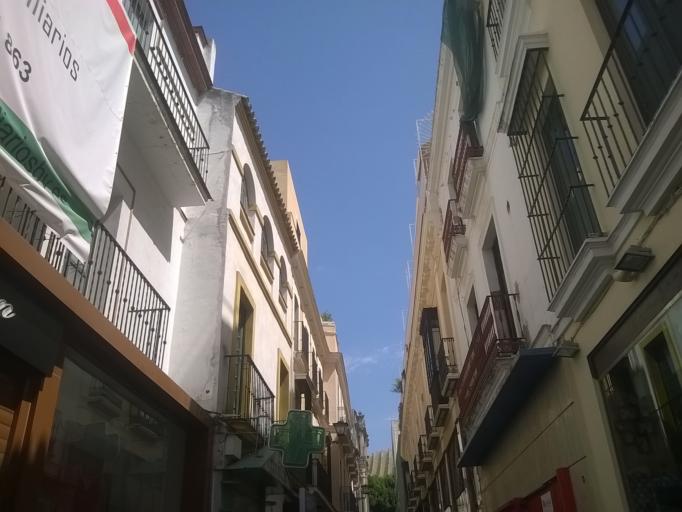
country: ES
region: Andalusia
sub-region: Provincia de Sevilla
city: Sevilla
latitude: 37.3913
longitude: -5.9922
